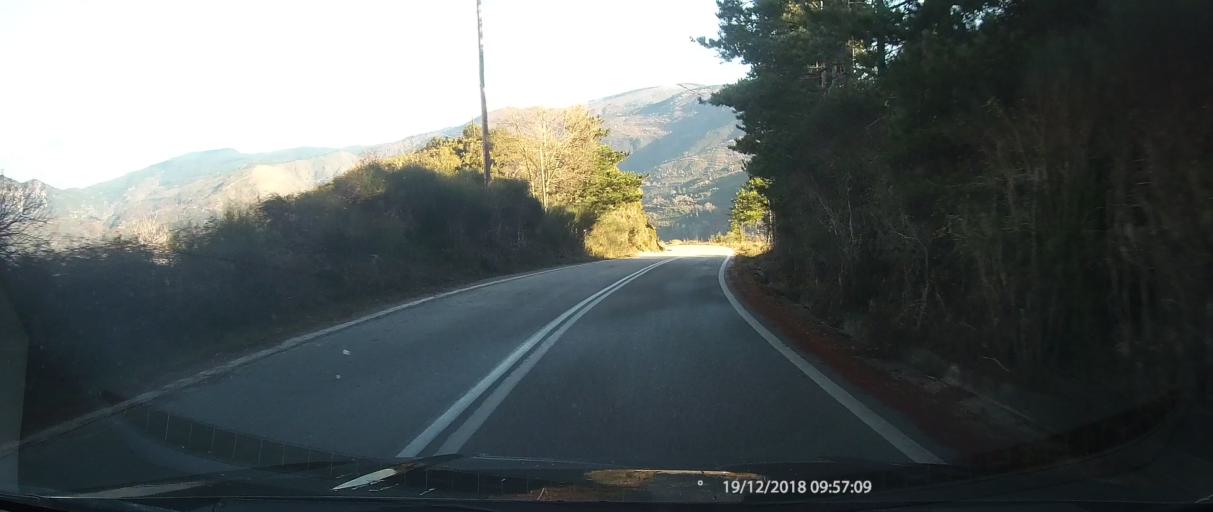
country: GR
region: Peloponnese
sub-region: Nomos Messinias
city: Paralia Vergas
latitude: 37.0869
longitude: 22.2372
